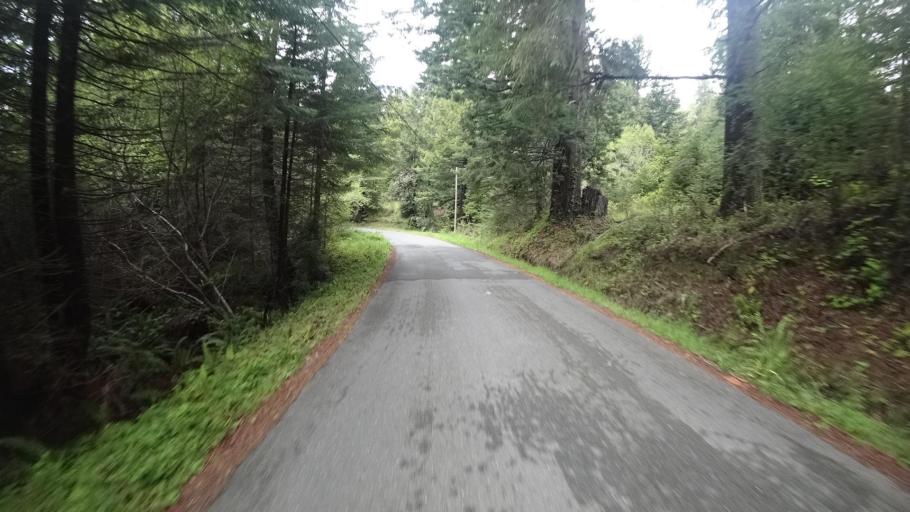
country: US
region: California
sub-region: Humboldt County
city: Blue Lake
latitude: 40.8556
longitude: -123.9303
